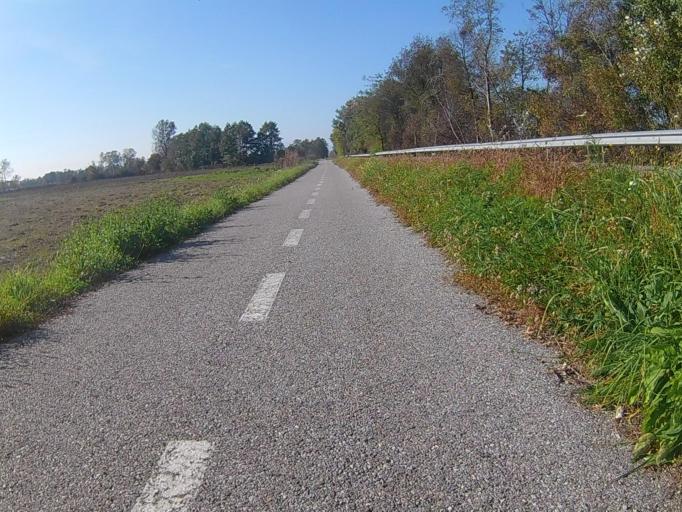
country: SI
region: Hajdina
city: Spodnja Hajdina
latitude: 46.4278
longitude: 15.8431
